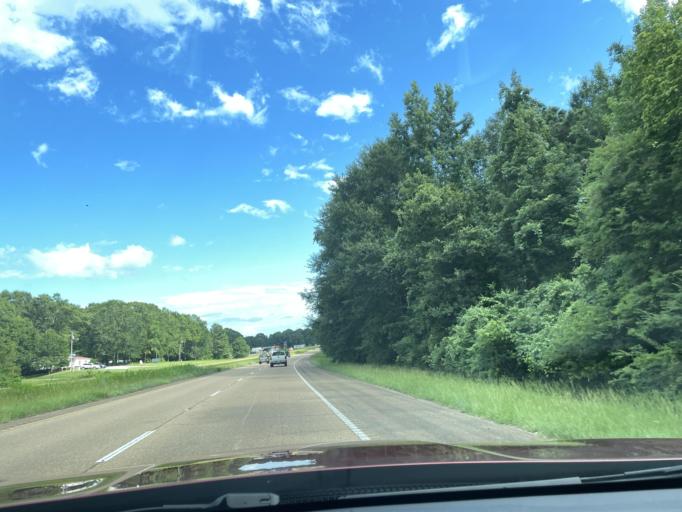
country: US
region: Mississippi
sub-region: Madison County
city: Flora
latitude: 32.5247
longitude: -90.3088
